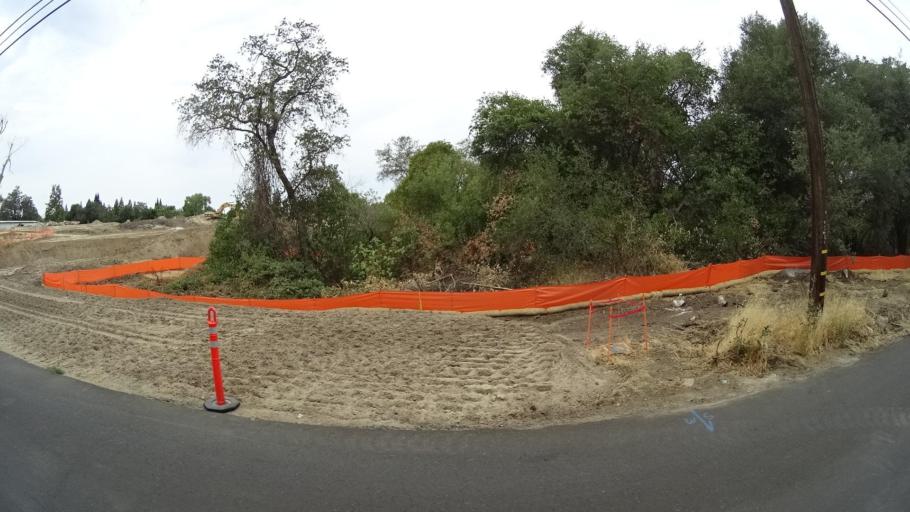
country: US
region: California
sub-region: Placer County
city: Rocklin
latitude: 38.7837
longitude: -121.2197
